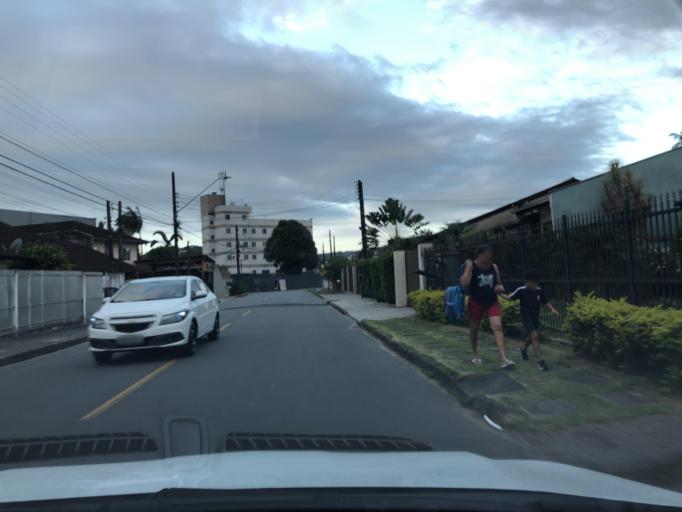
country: BR
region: Santa Catarina
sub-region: Joinville
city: Joinville
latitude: -26.2691
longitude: -48.8638
